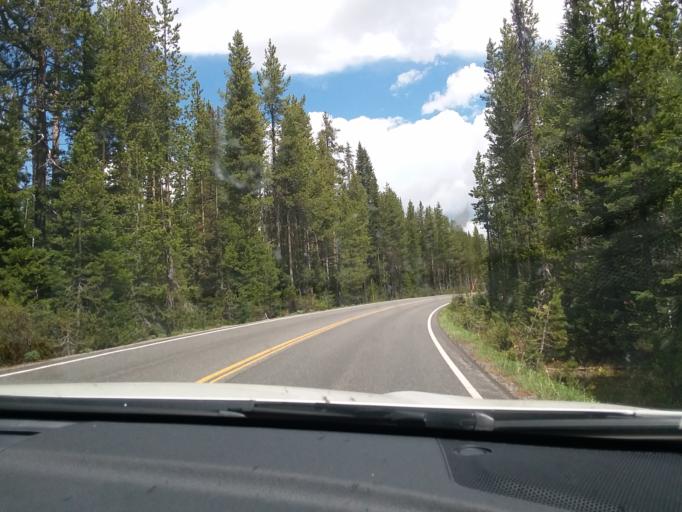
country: US
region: Idaho
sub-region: Teton County
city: Driggs
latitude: 44.1543
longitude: -110.6747
